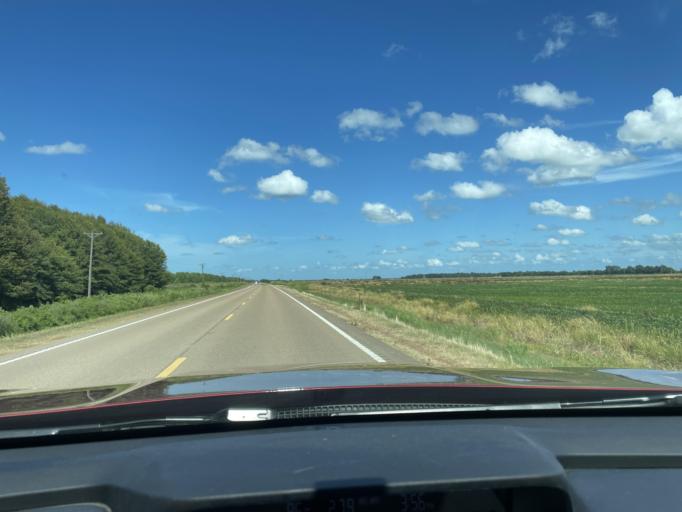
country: US
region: Mississippi
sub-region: Humphreys County
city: Belzoni
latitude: 33.1826
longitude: -90.6259
